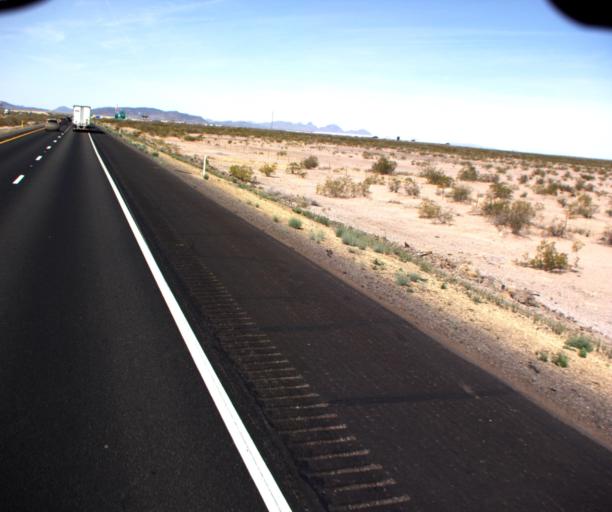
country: US
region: Arizona
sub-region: La Paz County
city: Salome
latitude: 33.6287
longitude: -113.7502
